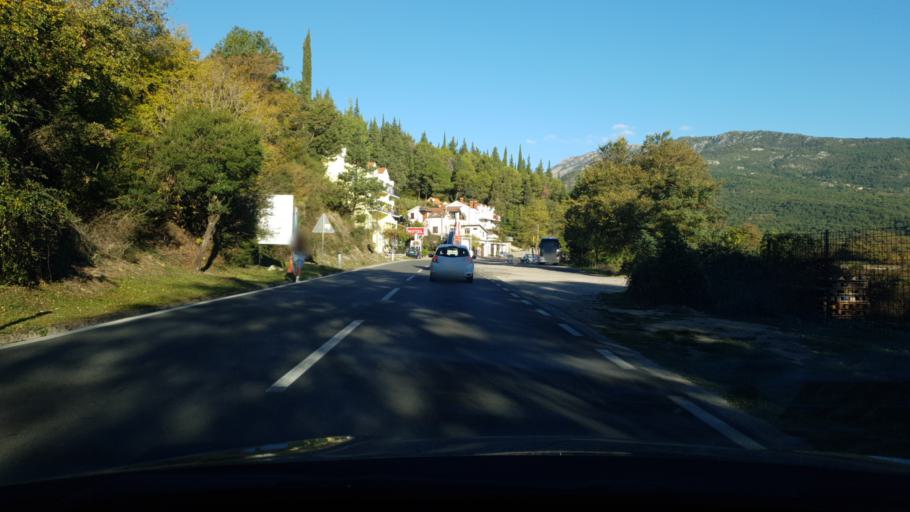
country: ME
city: Igalo
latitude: 42.4617
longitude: 18.4866
